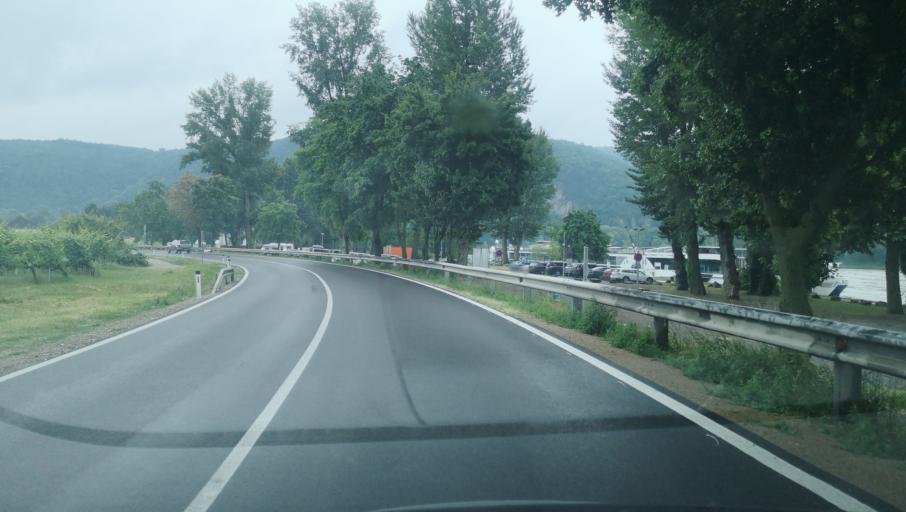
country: AT
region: Lower Austria
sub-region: Politischer Bezirk Krems
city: Durnstein
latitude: 48.3904
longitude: 15.5226
